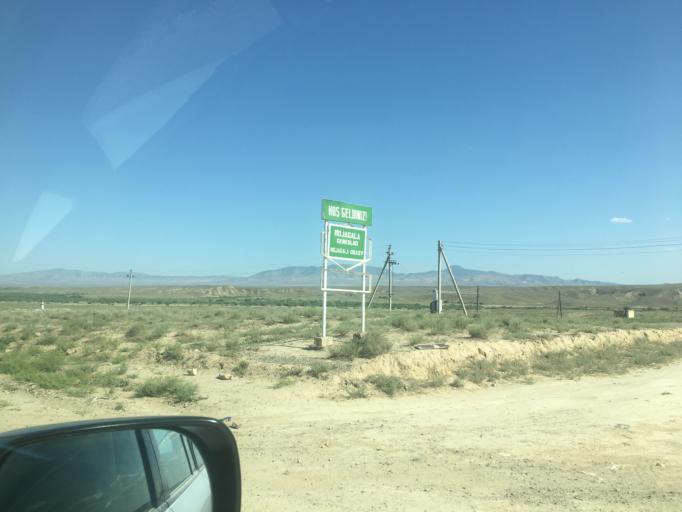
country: TM
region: Balkan
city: Serdar
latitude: 38.7223
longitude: 56.2939
